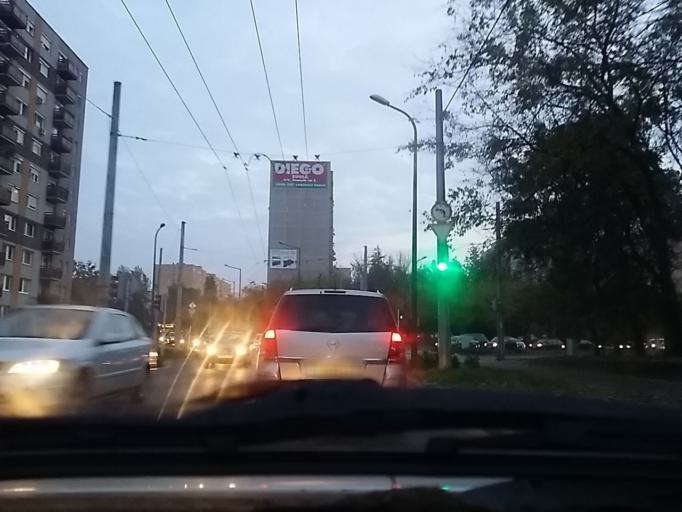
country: HU
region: Budapest
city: Budapest XVI. keruelet
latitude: 47.5118
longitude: 19.1466
